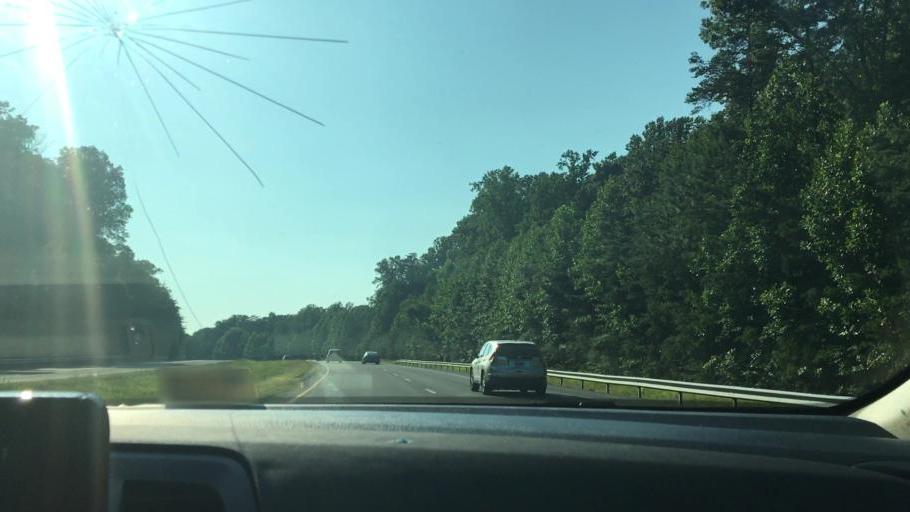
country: US
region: Virginia
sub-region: Prince William County
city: Buckhall
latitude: 38.6965
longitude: -77.3943
